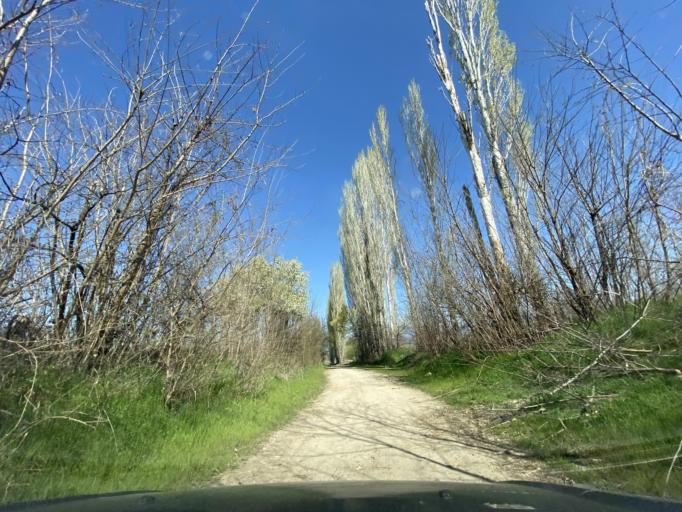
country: MK
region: Zrnovci
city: Zrnovci
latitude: 41.8568
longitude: 22.3887
